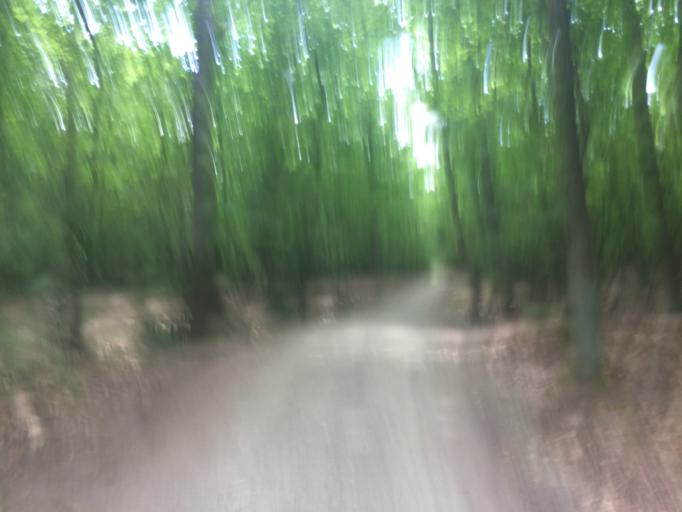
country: DK
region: Capital Region
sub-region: Bornholm Kommune
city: Ronne
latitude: 55.1294
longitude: 14.7153
